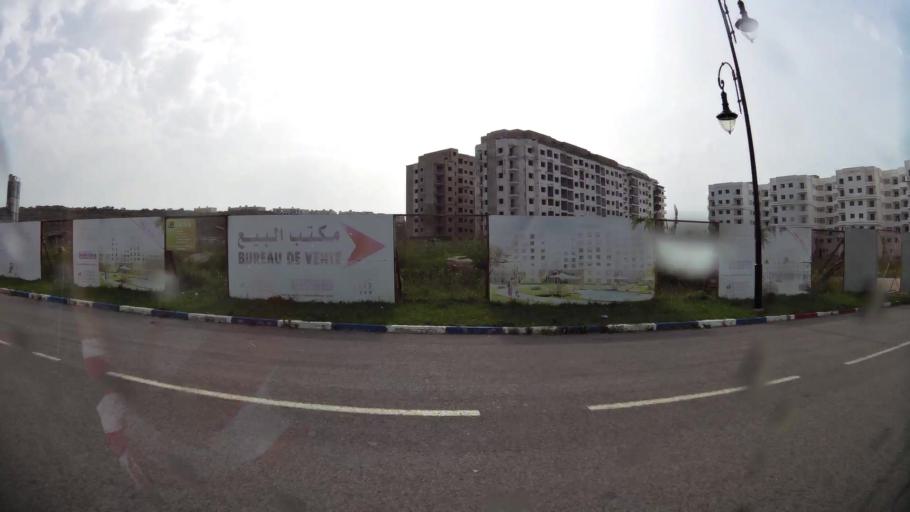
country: MA
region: Tanger-Tetouan
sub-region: Tanger-Assilah
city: Boukhalef
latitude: 35.7018
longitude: -5.9348
